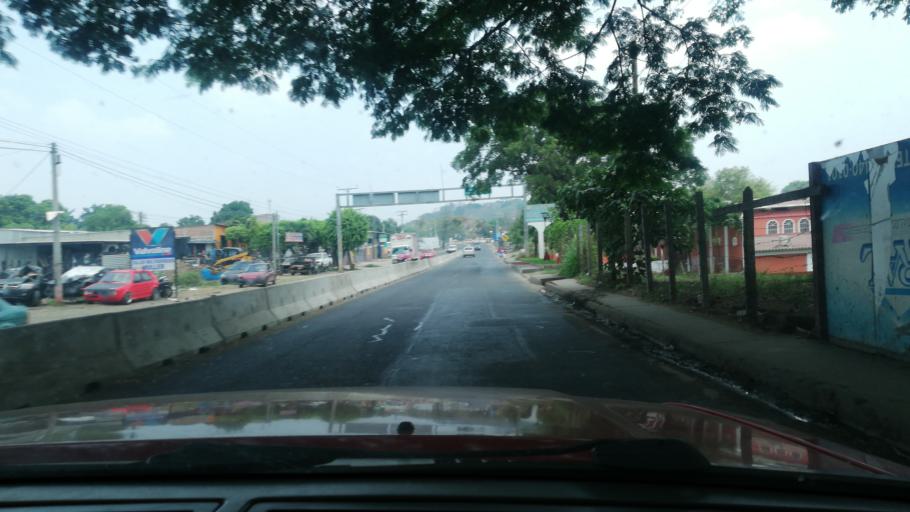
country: SV
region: Santa Ana
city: Santa Ana
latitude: 13.9744
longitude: -89.5869
